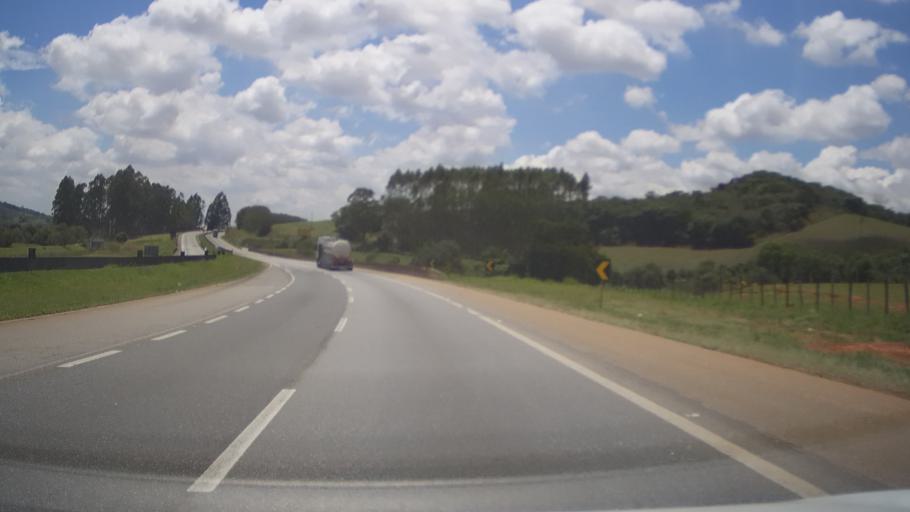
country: BR
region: Minas Gerais
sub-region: Campanha
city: Campanha
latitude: -21.8089
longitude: -45.4826
